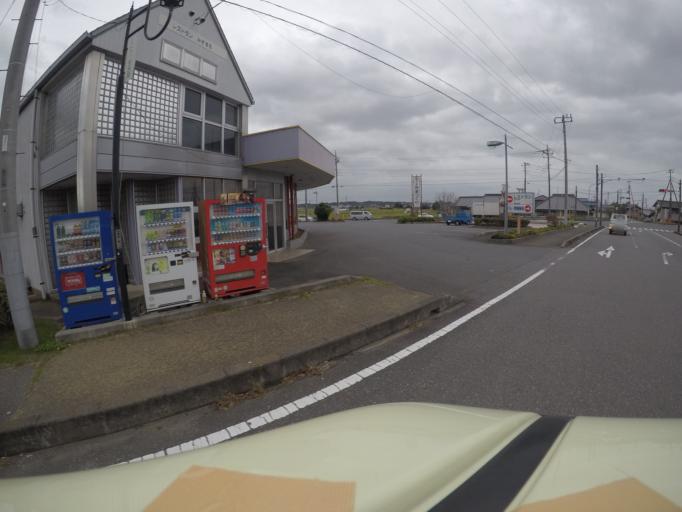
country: JP
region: Ibaraki
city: Inashiki
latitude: 36.0968
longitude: 140.4041
